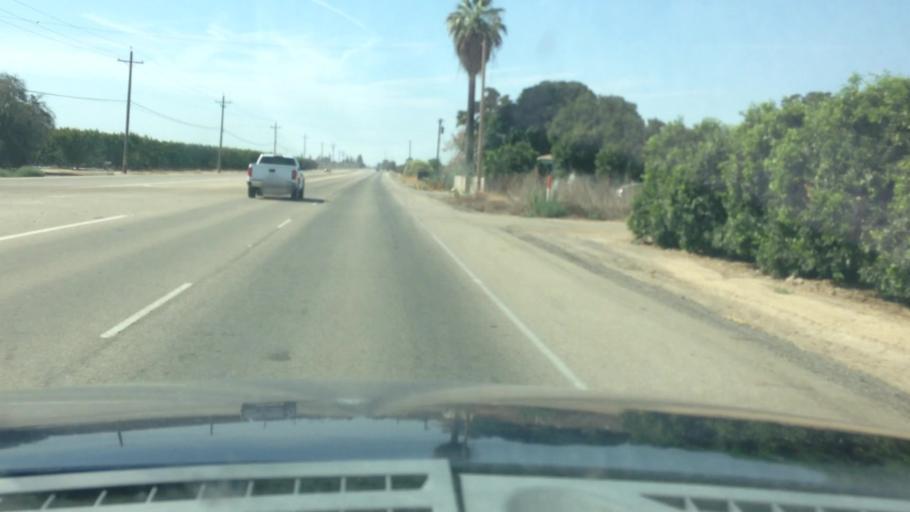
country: US
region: California
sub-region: Fresno County
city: Parlier
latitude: 36.6272
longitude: -119.5567
